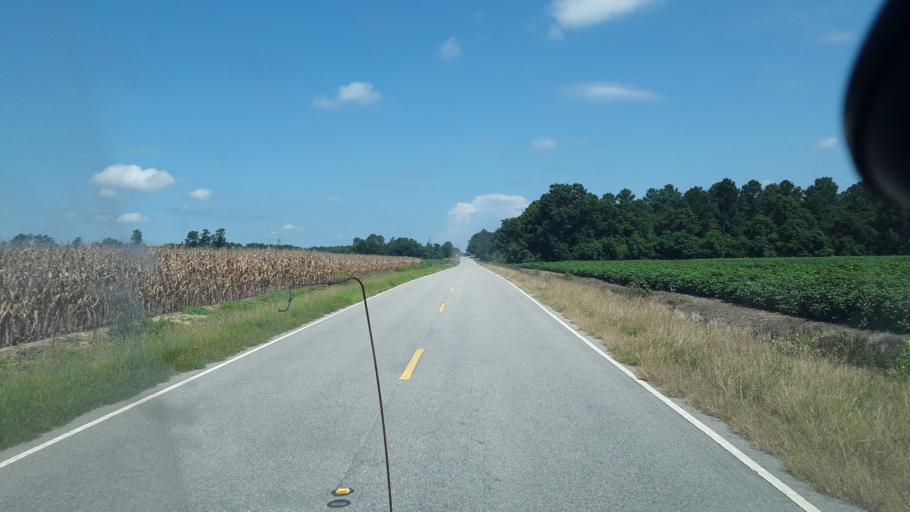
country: US
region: South Carolina
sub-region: Bamberg County
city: Bamberg
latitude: 33.4004
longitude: -81.0153
